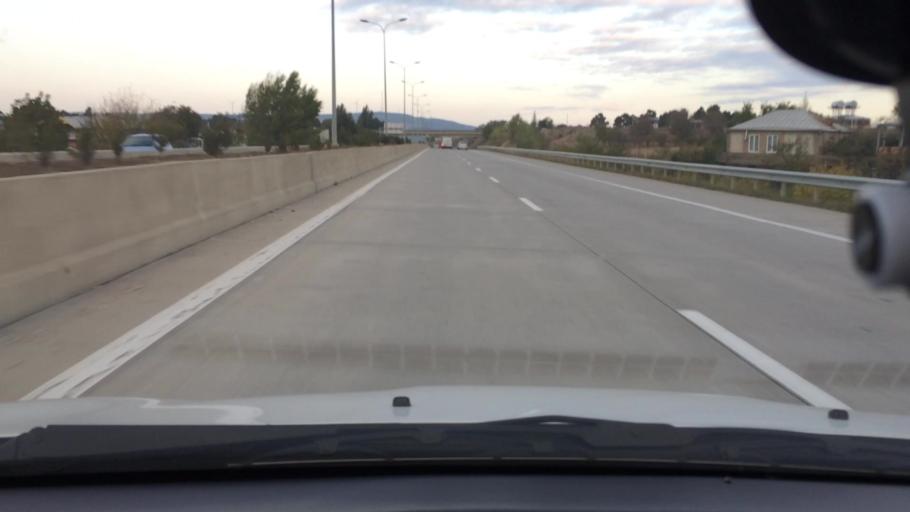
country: GE
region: Shida Kartli
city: Gori
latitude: 42.0174
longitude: 44.1341
